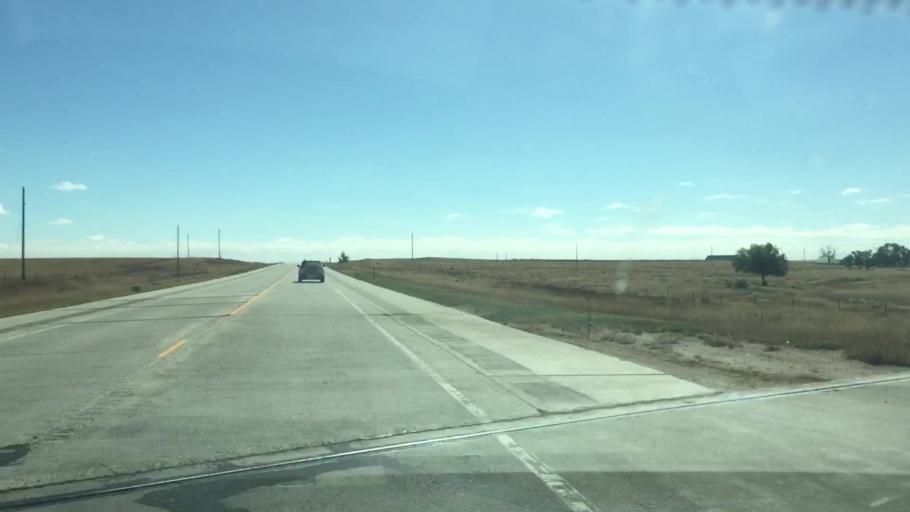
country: US
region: Colorado
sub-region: Lincoln County
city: Hugo
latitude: 39.1992
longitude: -103.5767
